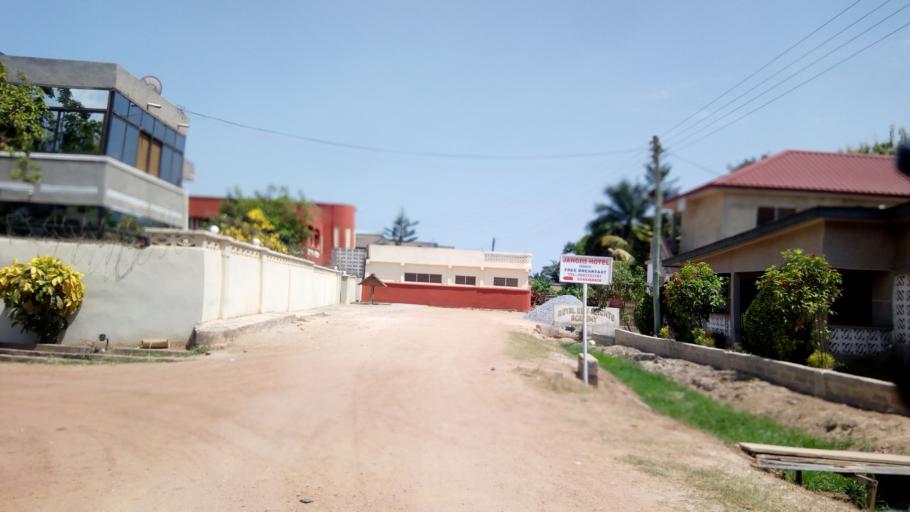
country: GH
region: Central
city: Cape Coast
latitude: 5.1316
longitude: -1.2819
